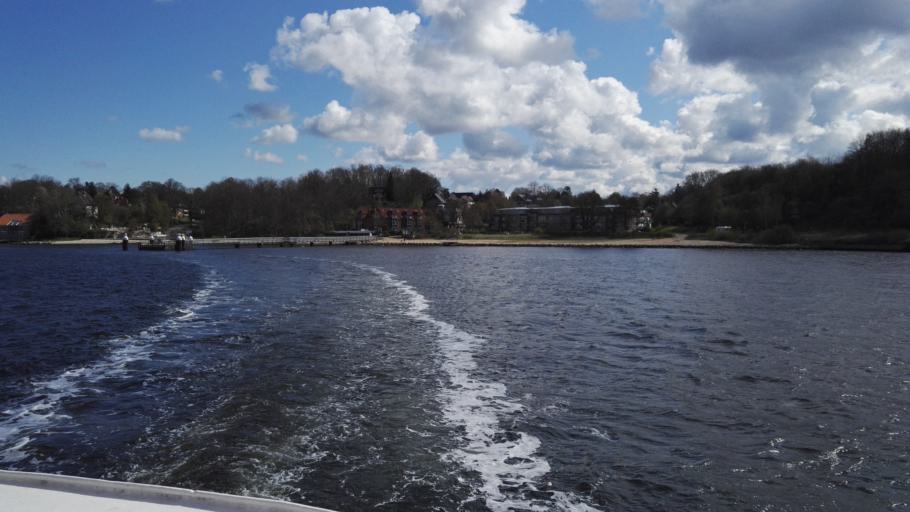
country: DE
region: Schleswig-Holstein
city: Monkeberg
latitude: 54.3510
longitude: 10.1739
